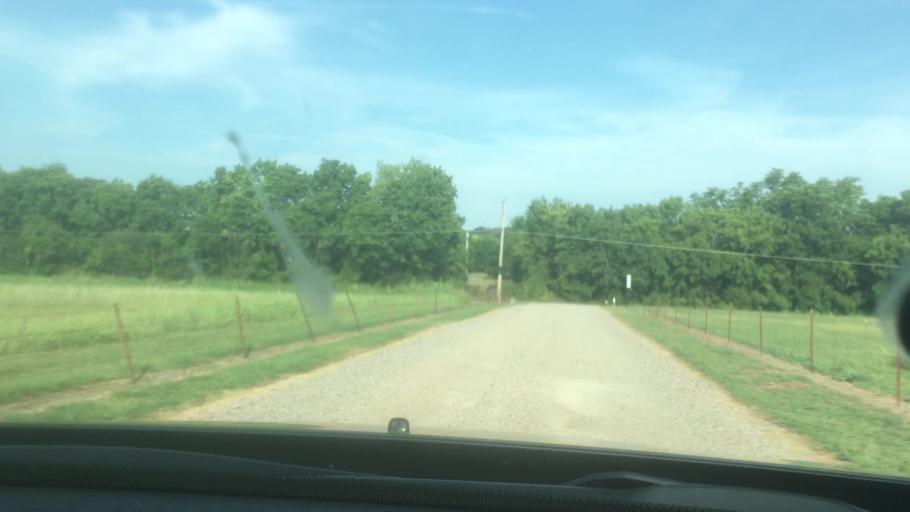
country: US
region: Oklahoma
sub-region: Pontotoc County
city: Ada
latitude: 34.7219
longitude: -96.6691
